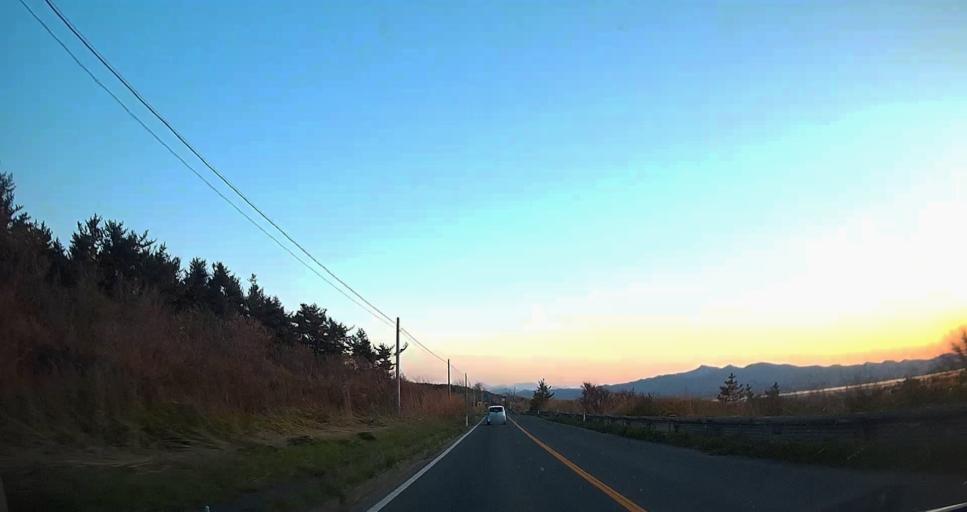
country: JP
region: Aomori
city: Misawa
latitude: 40.8888
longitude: 141.1625
